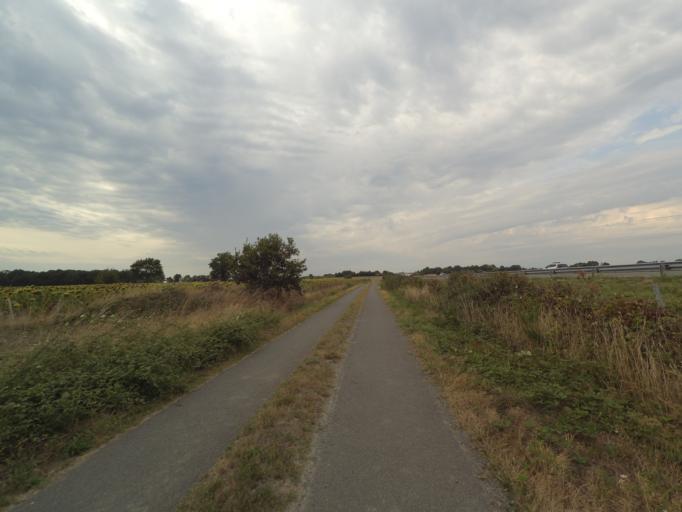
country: FR
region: Pays de la Loire
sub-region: Departement de la Vendee
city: Bouffere
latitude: 46.9898
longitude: -1.3816
